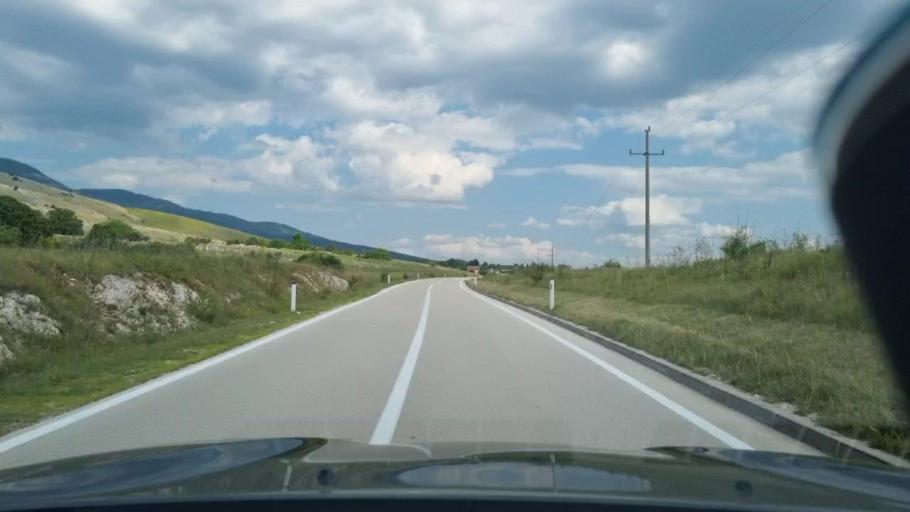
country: BA
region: Federation of Bosnia and Herzegovina
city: Bosansko Grahovo
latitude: 44.1270
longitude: 16.5178
